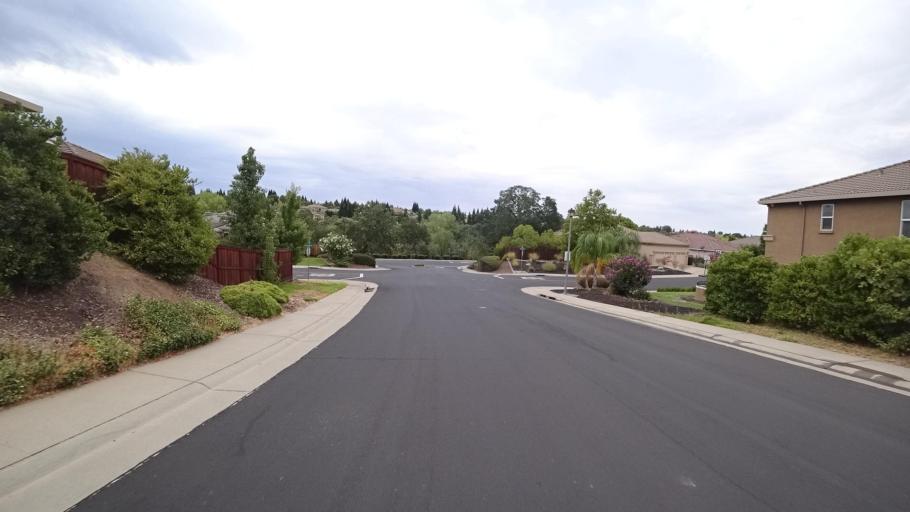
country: US
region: California
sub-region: Placer County
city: Rocklin
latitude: 38.7728
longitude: -121.2250
